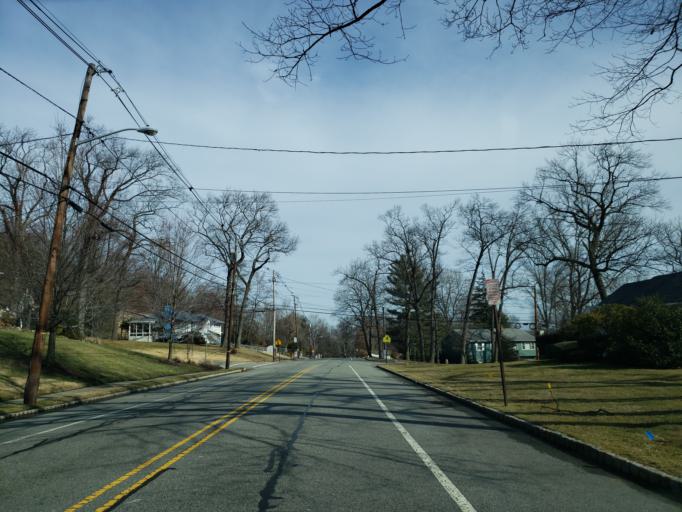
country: US
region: New Jersey
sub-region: Essex County
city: Cedar Grove
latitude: 40.8571
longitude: -74.2397
